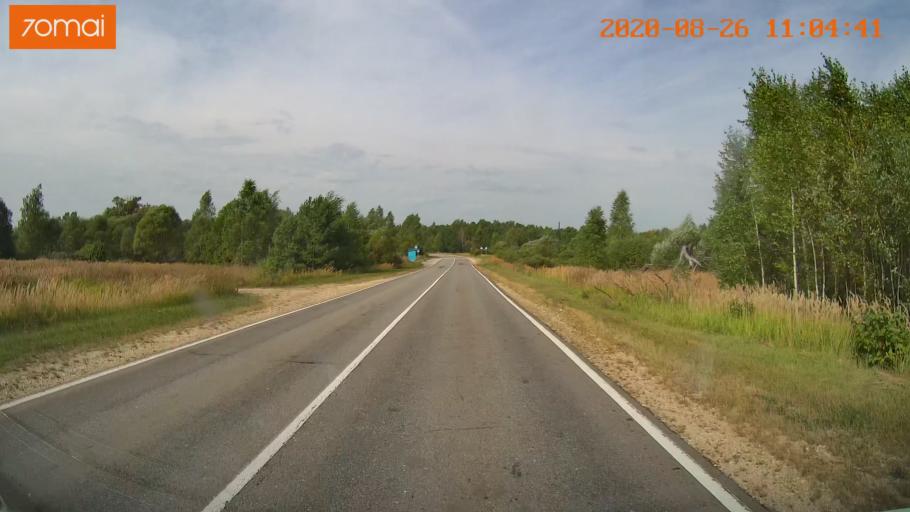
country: RU
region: Rjazan
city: Izhevskoye
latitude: 54.5290
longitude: 41.1906
